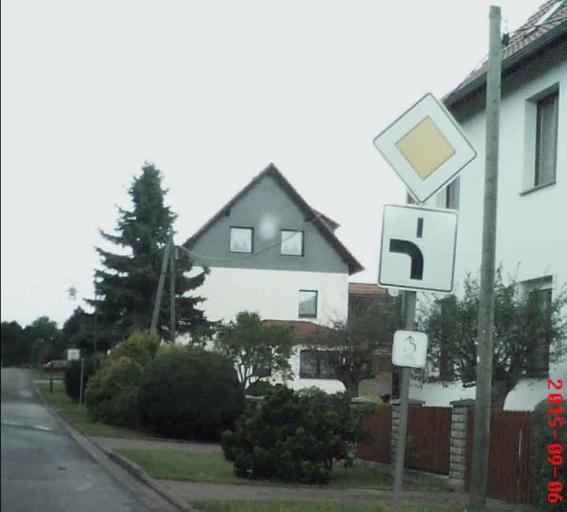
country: DE
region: Thuringia
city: Weissenborn-Luderode
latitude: 51.5551
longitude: 10.3751
